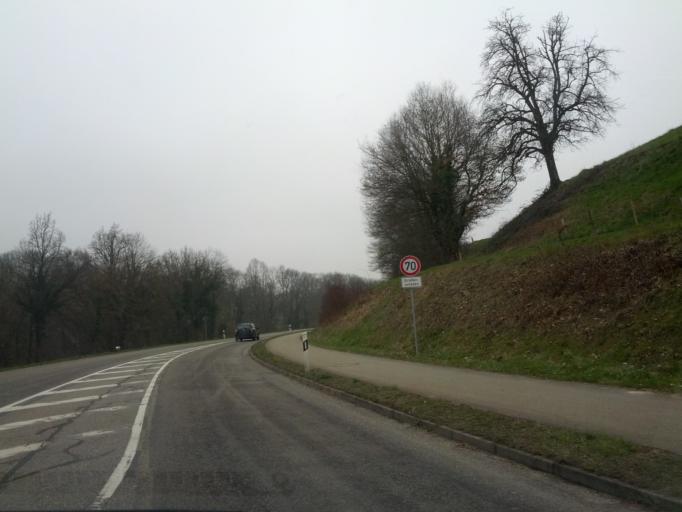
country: DE
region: Baden-Wuerttemberg
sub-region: Freiburg Region
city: Au
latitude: 47.9520
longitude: 7.8276
